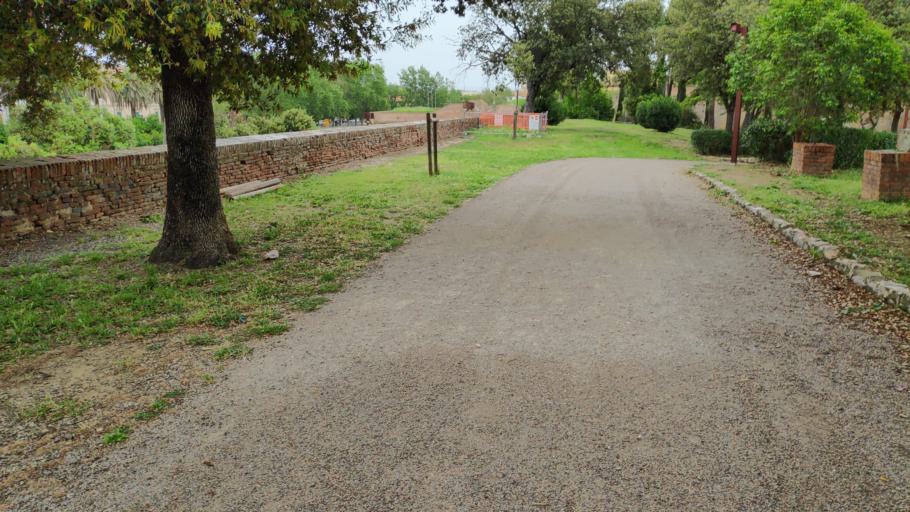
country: IT
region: Tuscany
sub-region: Provincia di Grosseto
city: Grosseto
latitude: 42.7624
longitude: 11.1155
